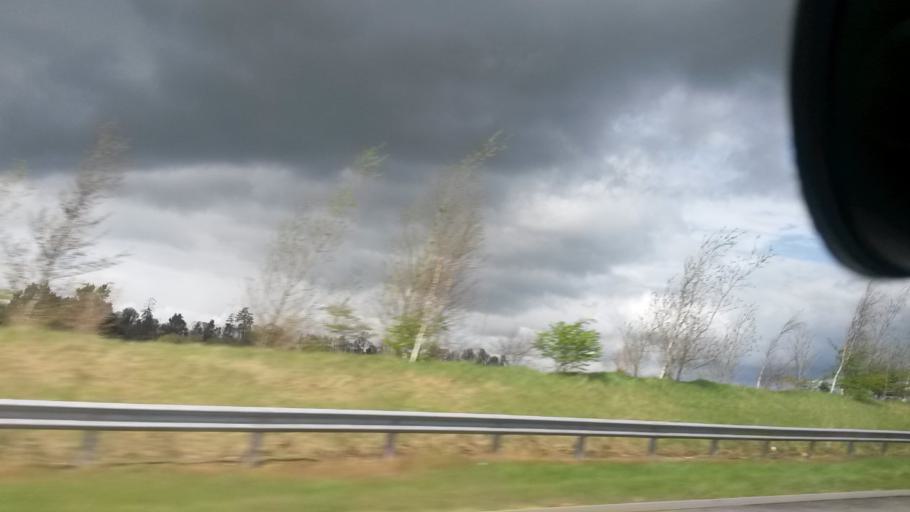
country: IE
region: Leinster
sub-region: Laois
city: Rathdowney
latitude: 52.8610
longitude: -7.4850
